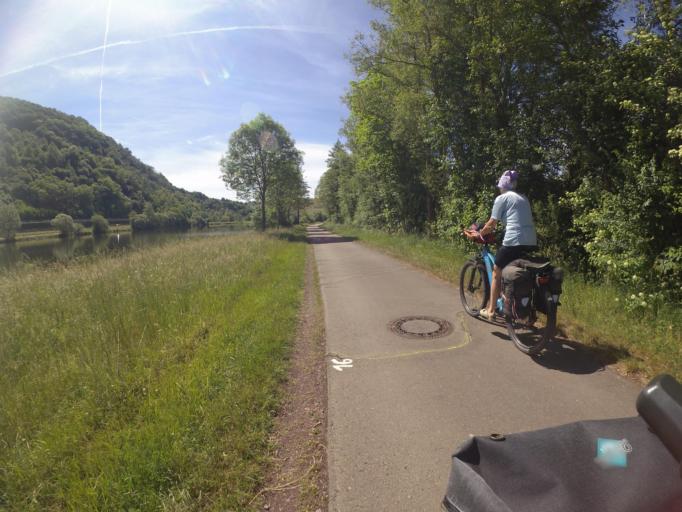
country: DE
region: Rheinland-Pfalz
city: Schoden
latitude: 49.6308
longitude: 6.5741
